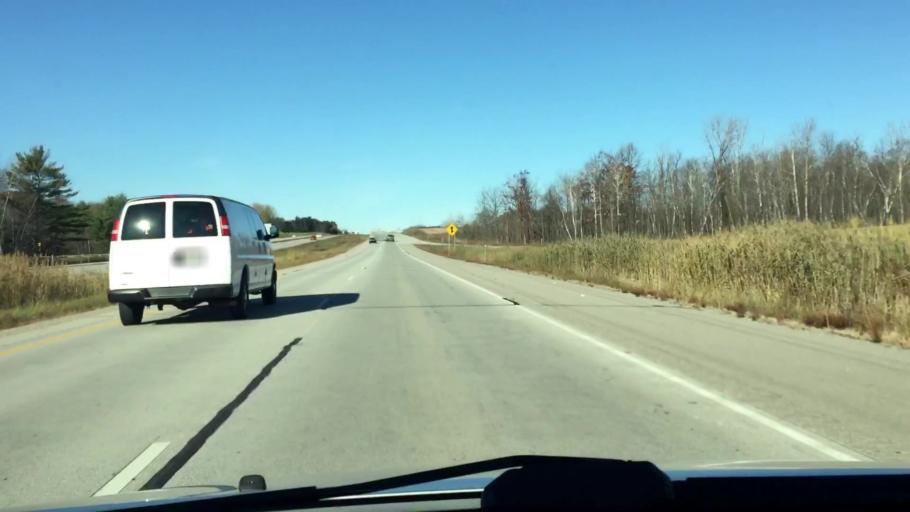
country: US
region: Wisconsin
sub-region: Brown County
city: Howard
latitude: 44.5613
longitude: -88.1322
